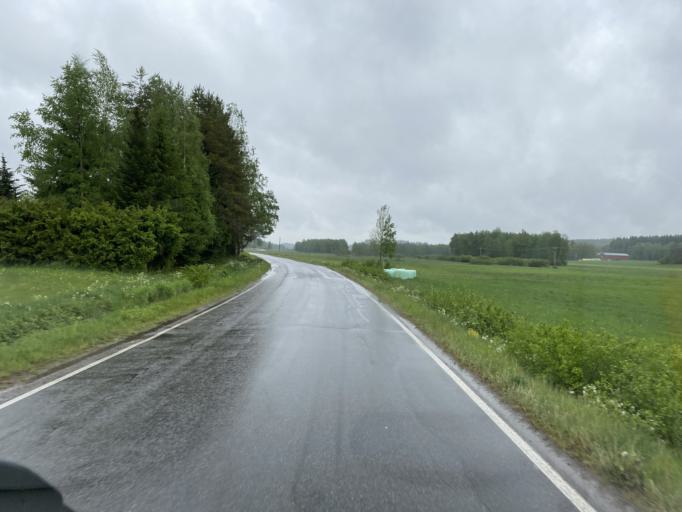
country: FI
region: Haeme
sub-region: Forssa
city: Humppila
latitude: 61.0419
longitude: 23.3965
